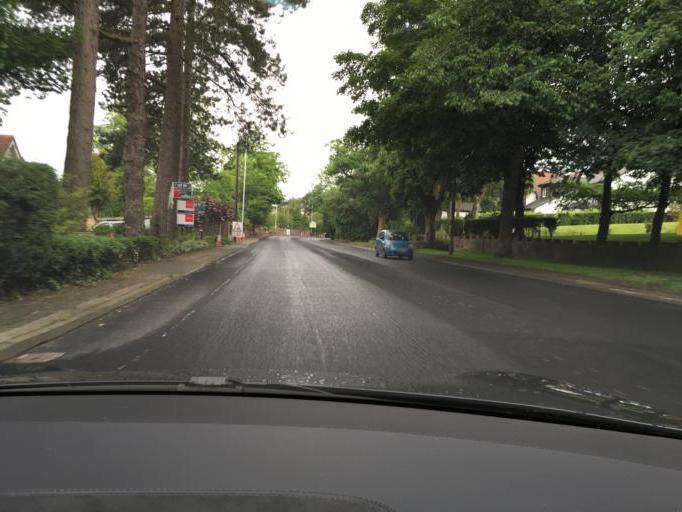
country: GB
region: England
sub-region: Cheshire East
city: Disley
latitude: 53.3604
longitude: -2.0566
